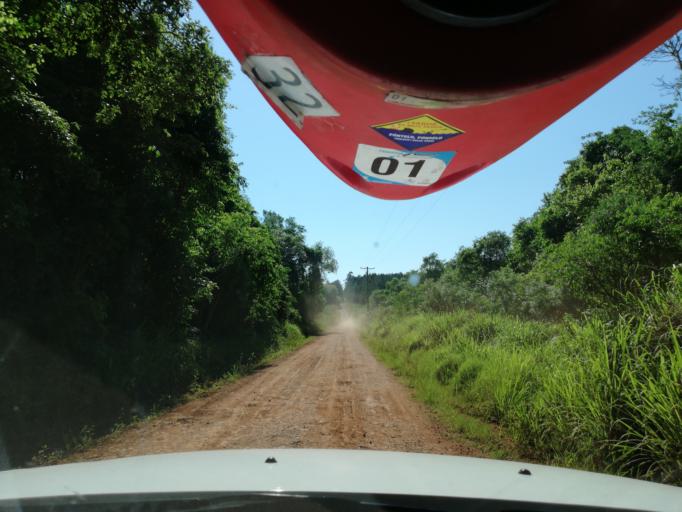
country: AR
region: Misiones
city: Puerto Leoni
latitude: -26.9695
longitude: -55.1635
